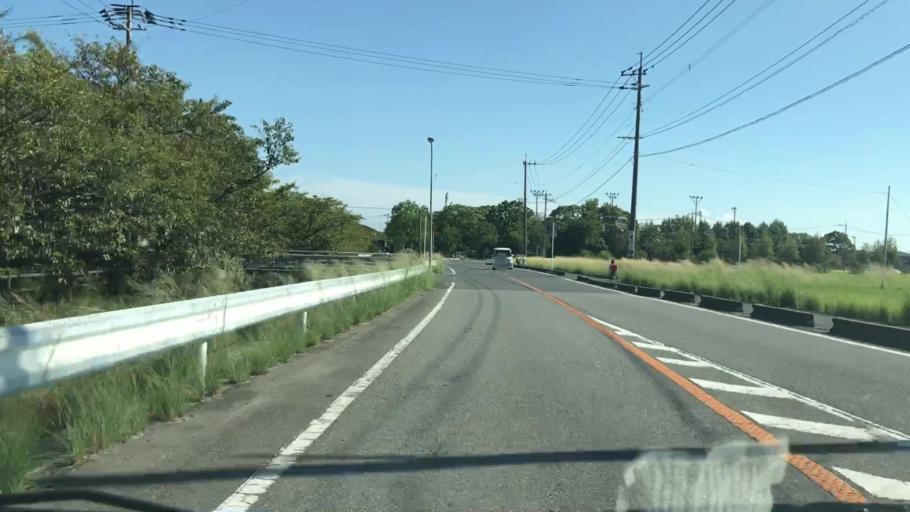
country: JP
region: Saga Prefecture
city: Okawa
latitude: 33.2291
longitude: 130.3558
